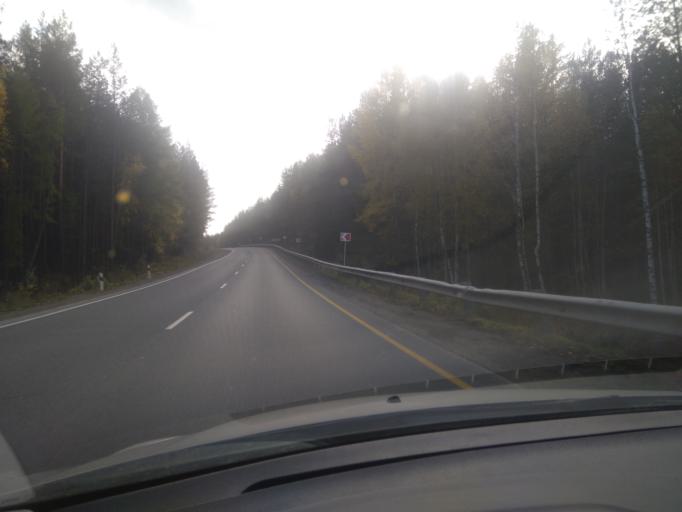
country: RU
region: Sverdlovsk
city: Neyvo-Rudyanka
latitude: 57.3161
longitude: 60.2544
